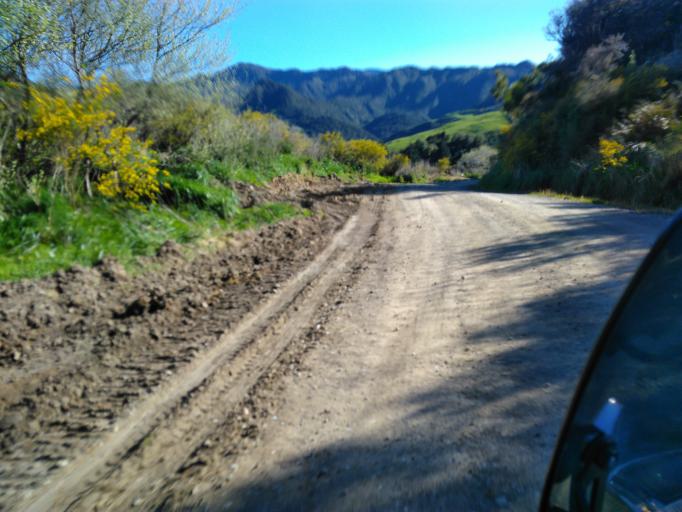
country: NZ
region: Gisborne
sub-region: Gisborne District
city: Gisborne
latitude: -38.3963
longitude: 177.6671
